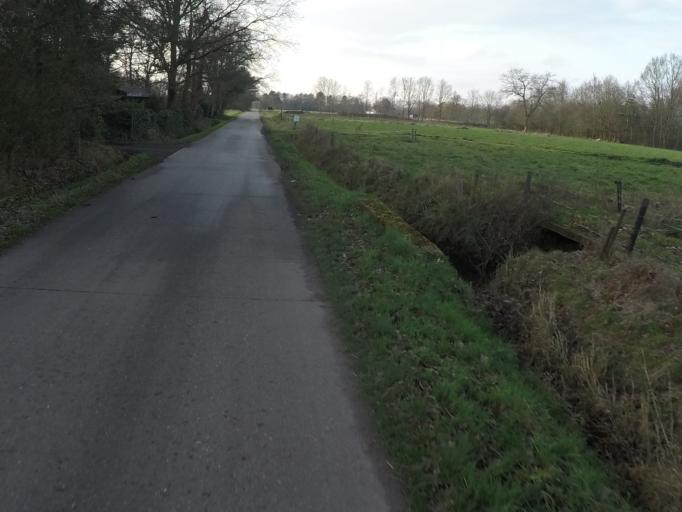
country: BE
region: Flanders
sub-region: Provincie Antwerpen
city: Putte
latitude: 51.0309
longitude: 4.6750
